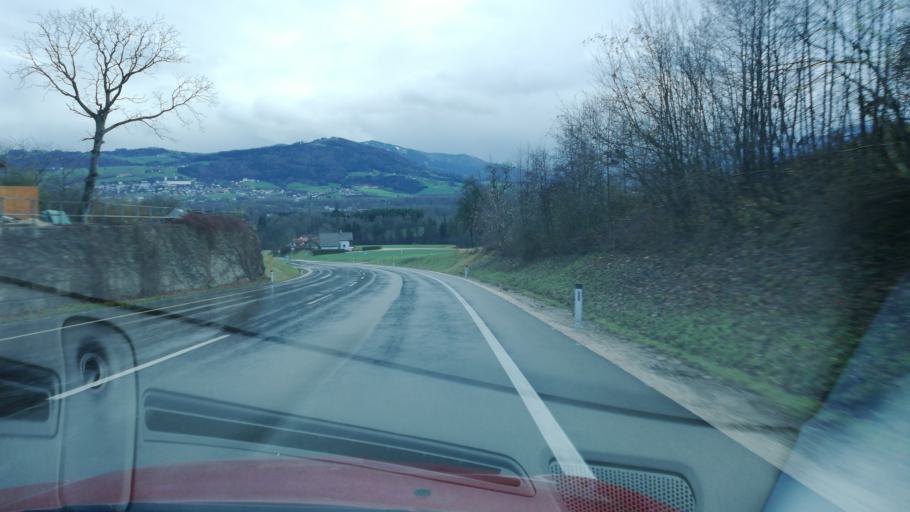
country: AT
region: Upper Austria
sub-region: Politischer Bezirk Kirchdorf an der Krems
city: Micheldorf in Oberoesterreich
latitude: 47.9573
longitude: 14.0819
